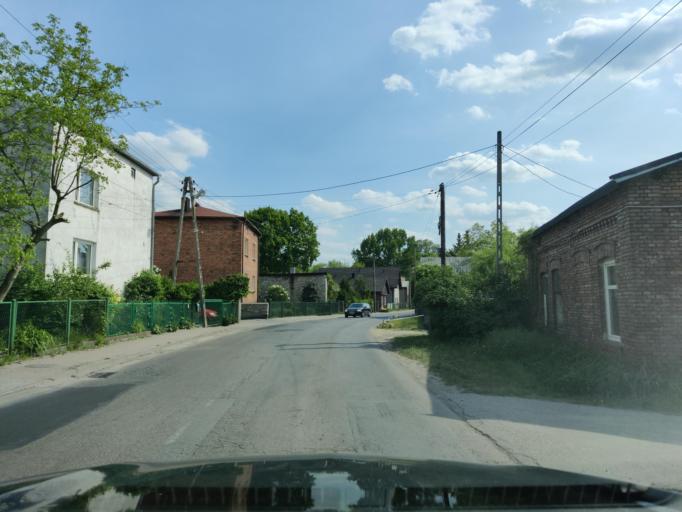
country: PL
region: Silesian Voivodeship
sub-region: Dabrowa Gornicza
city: Dabrowa Gornicza
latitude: 50.3926
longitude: 19.2417
